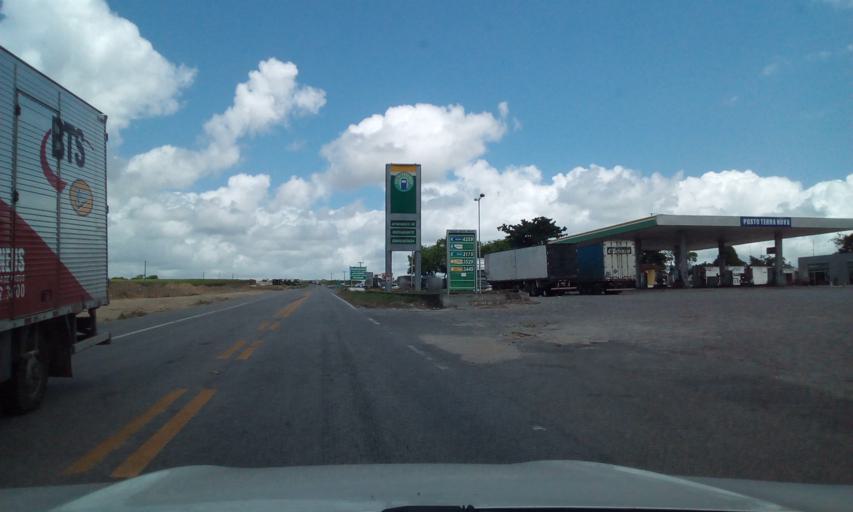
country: BR
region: Alagoas
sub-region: Pilar
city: Pilar
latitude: -9.5868
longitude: -35.9863
